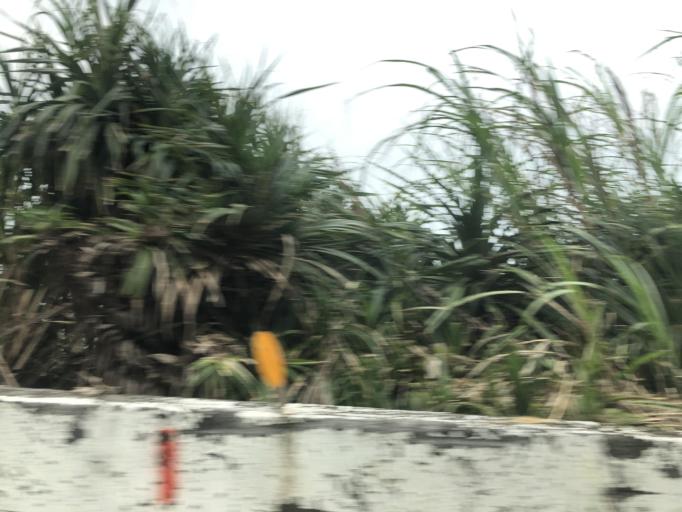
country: TW
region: Taiwan
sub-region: Keelung
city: Keelung
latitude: 25.2046
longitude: 121.6826
